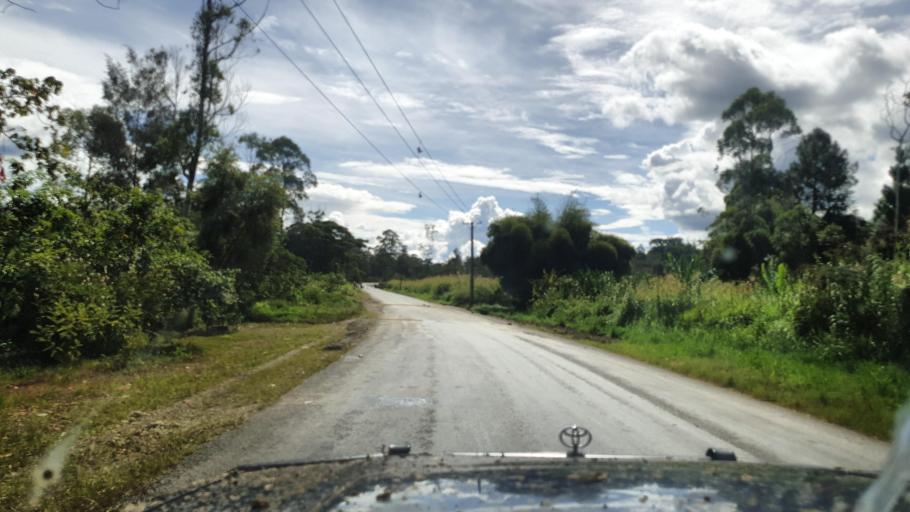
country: PG
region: Jiwaka
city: Minj
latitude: -5.8852
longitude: 144.7289
